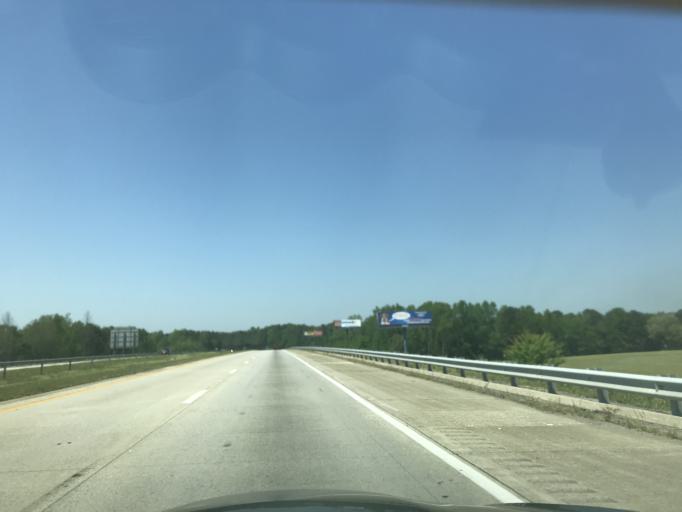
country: US
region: North Carolina
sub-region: Johnston County
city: Benson
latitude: 35.4072
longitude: -78.5238
